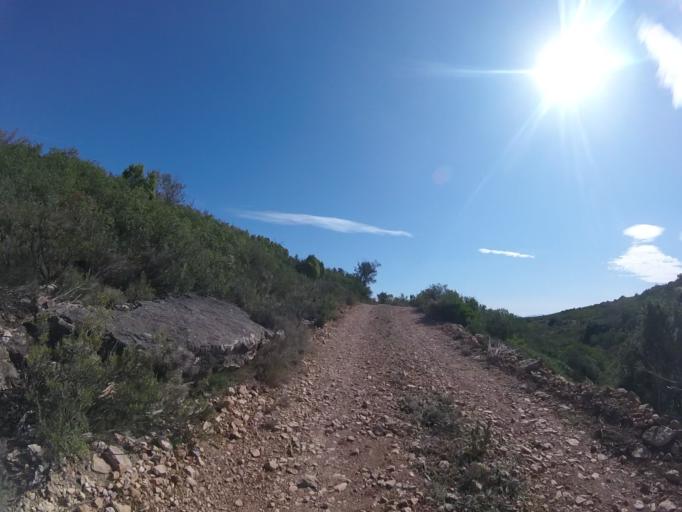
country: ES
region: Valencia
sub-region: Provincia de Castello
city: Sarratella
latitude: 40.2723
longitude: 0.0252
